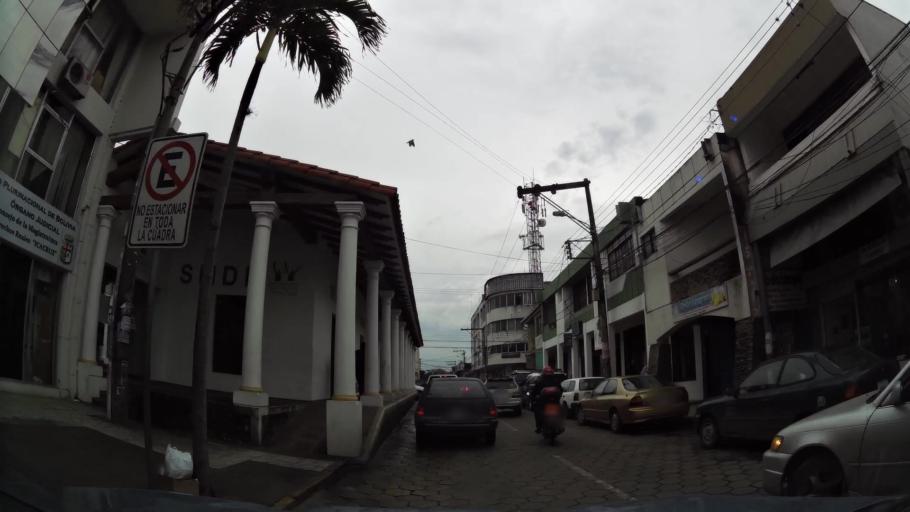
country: BO
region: Santa Cruz
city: Santa Cruz de la Sierra
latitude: -17.7779
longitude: -63.1820
